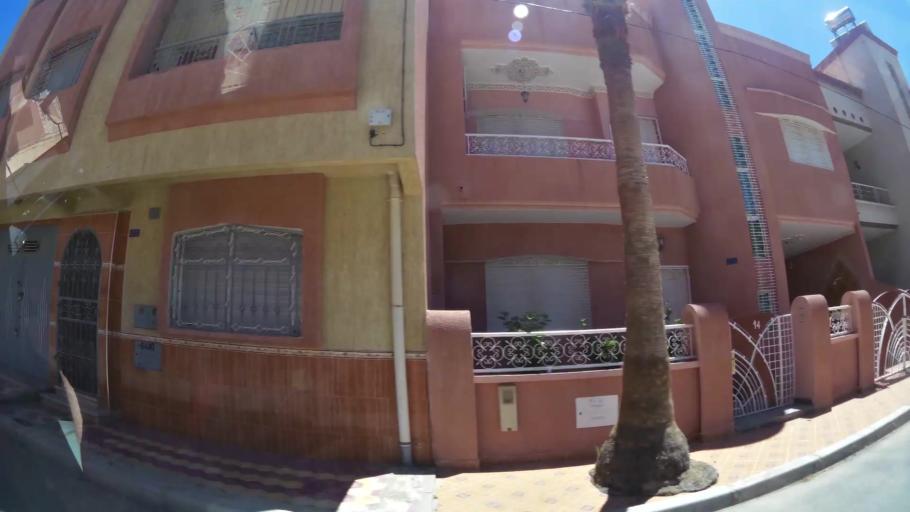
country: MA
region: Oriental
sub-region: Berkane-Taourirt
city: Madagh
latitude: 35.0794
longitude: -2.2268
